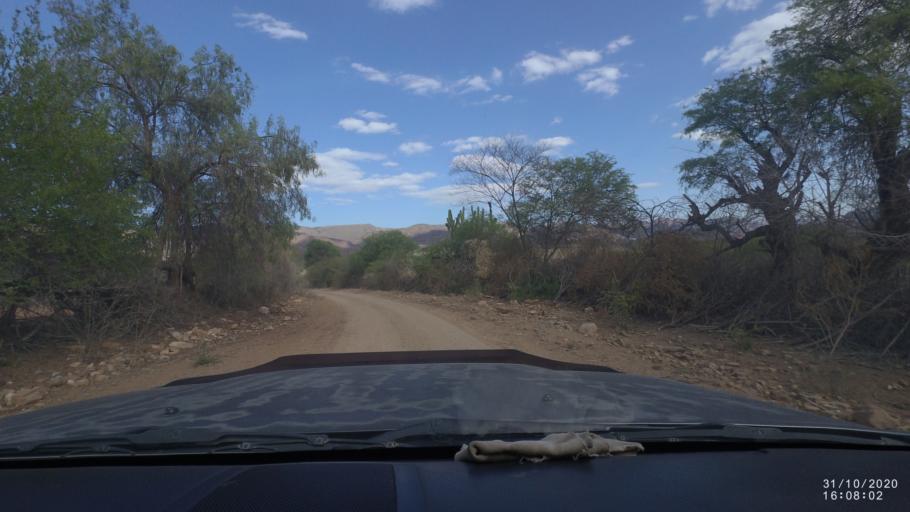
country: BO
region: Chuquisaca
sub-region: Provincia Zudanez
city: Mojocoya
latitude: -18.3838
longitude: -64.6431
